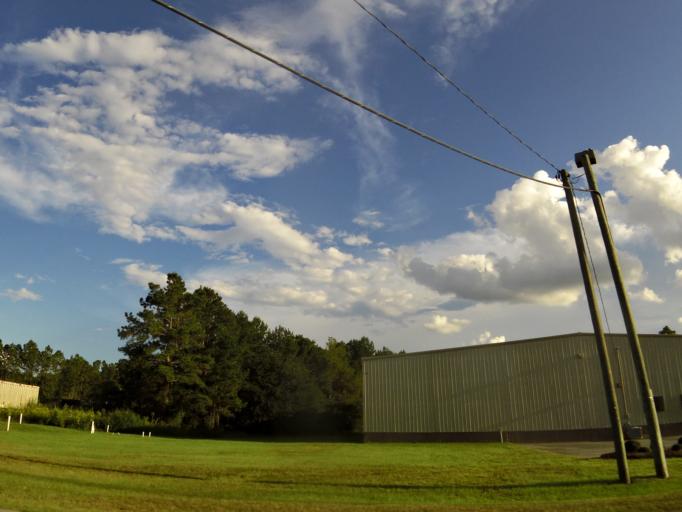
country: US
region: Georgia
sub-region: Lowndes County
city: Remerton
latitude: 30.8180
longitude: -83.3080
